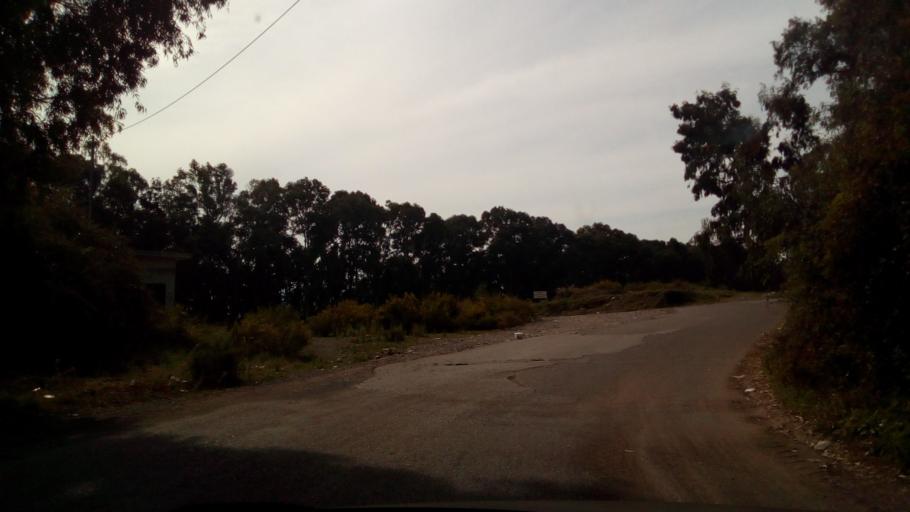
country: GR
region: West Greece
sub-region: Nomos Aitolias kai Akarnanias
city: Nafpaktos
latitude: 38.3989
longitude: 21.8682
